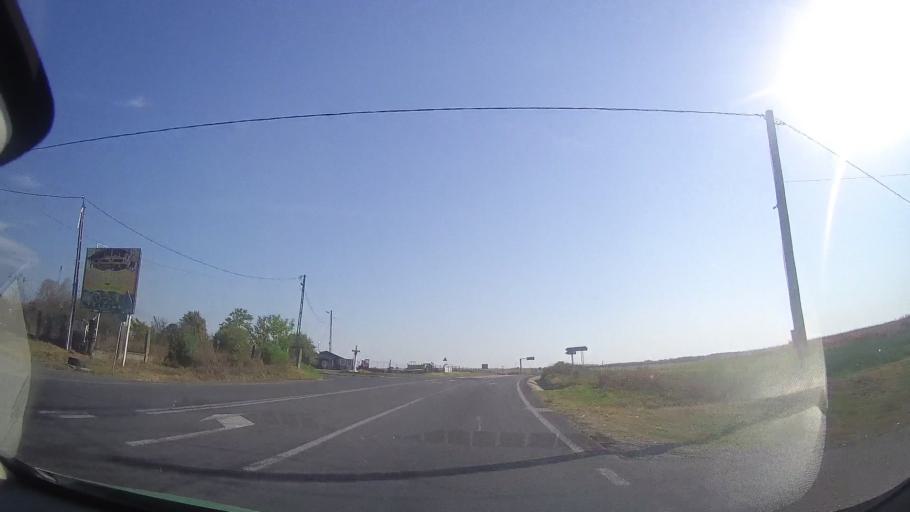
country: RO
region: Timis
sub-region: Comuna Topolovatu Mare
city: Topolovatu Mare
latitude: 45.7747
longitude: 21.6286
